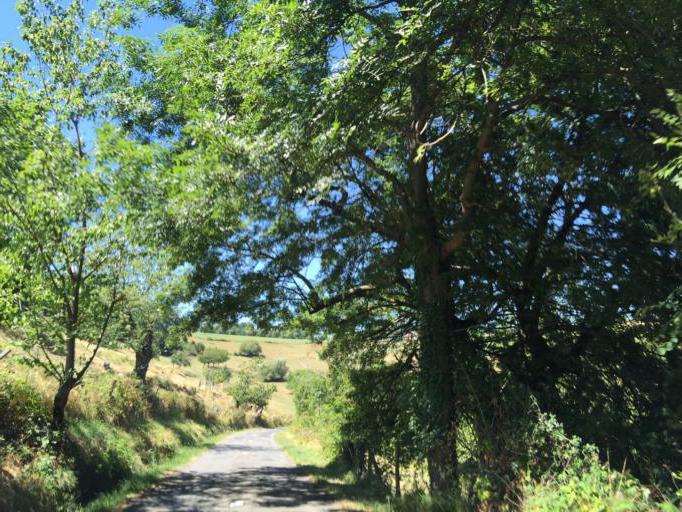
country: FR
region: Rhone-Alpes
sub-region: Departement de la Loire
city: Saint-Jean-Bonnefonds
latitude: 45.4670
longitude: 4.4644
